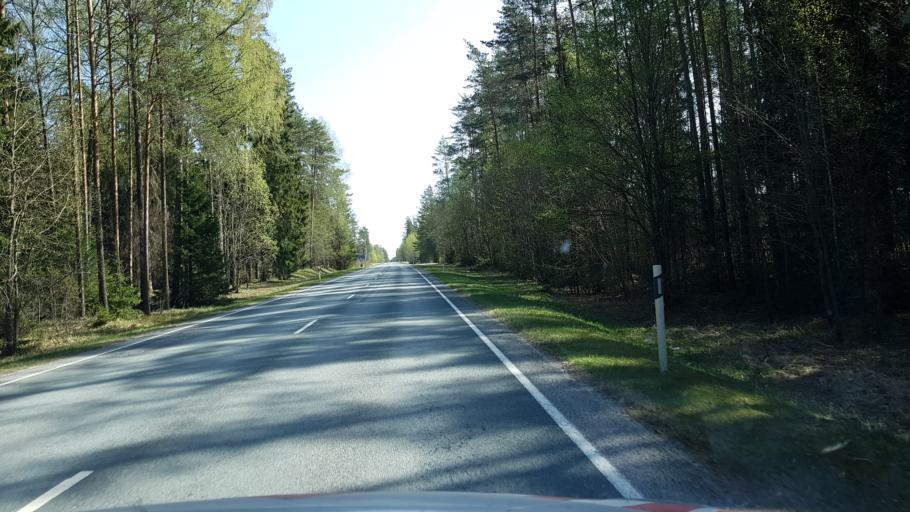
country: EE
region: Viljandimaa
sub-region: Moisakuela linn
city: Moisakula
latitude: 58.2476
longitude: 25.1632
